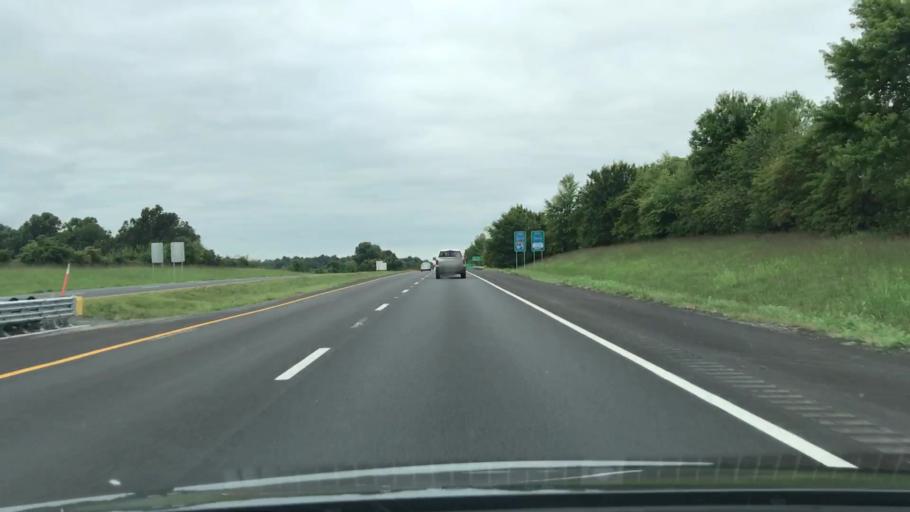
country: US
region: Kentucky
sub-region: Graves County
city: Mayfield
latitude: 36.7220
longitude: -88.6851
